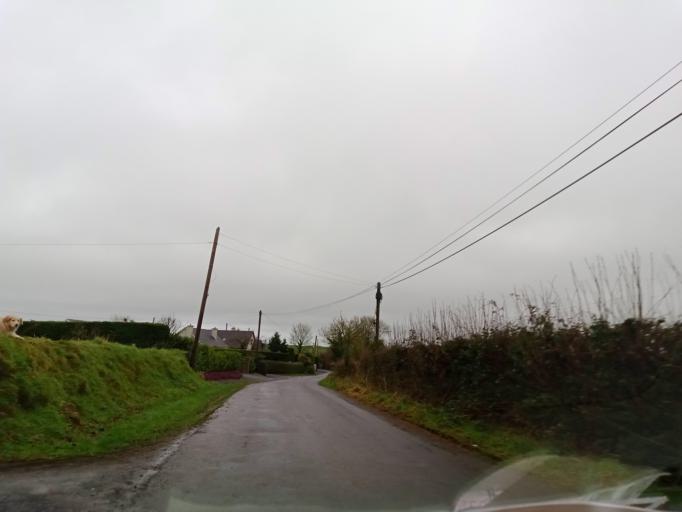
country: IE
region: Munster
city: Fethard
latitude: 52.5608
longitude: -7.6930
